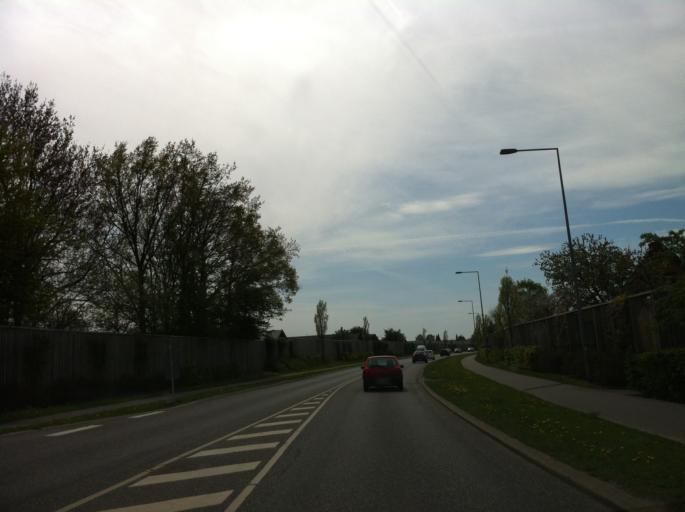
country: DK
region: Zealand
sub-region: Naestved Kommune
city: Naestved
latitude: 55.2188
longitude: 11.7753
